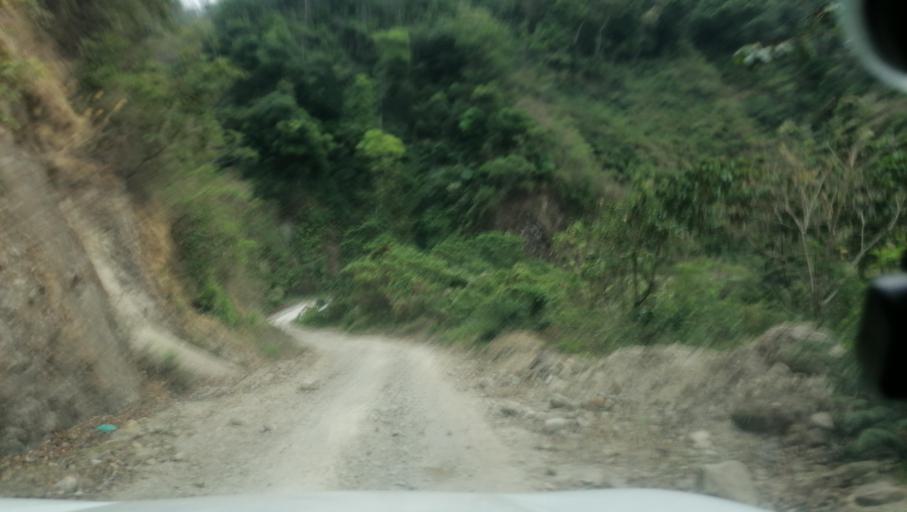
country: MX
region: Chiapas
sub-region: Cacahoatan
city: Benito Juarez
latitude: 15.1671
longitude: -92.1662
